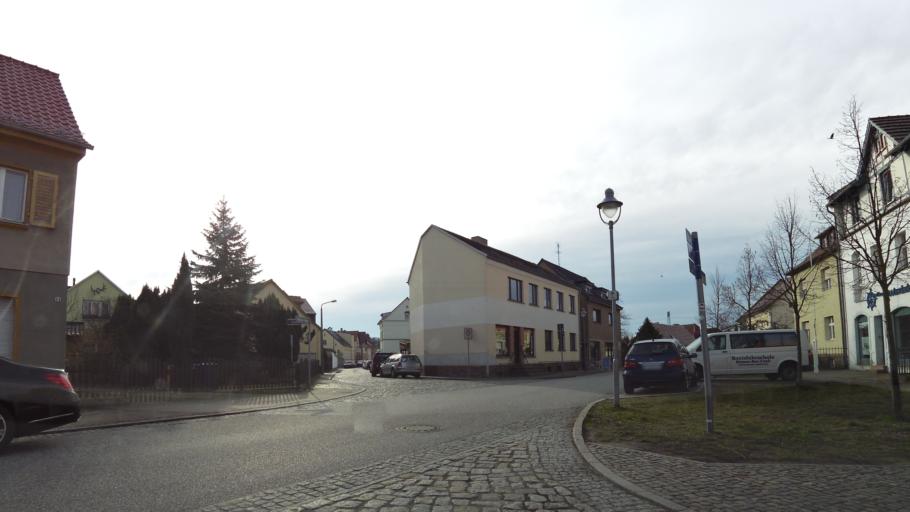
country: DE
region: Brandenburg
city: Michendorf
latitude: 52.3477
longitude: 12.9904
